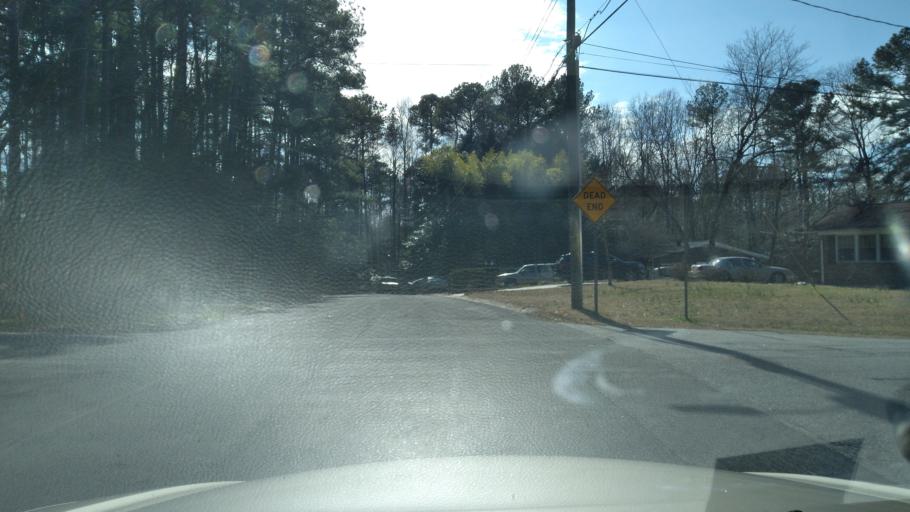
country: US
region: North Carolina
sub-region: Wake County
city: Garner
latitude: 35.6968
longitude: -78.6343
